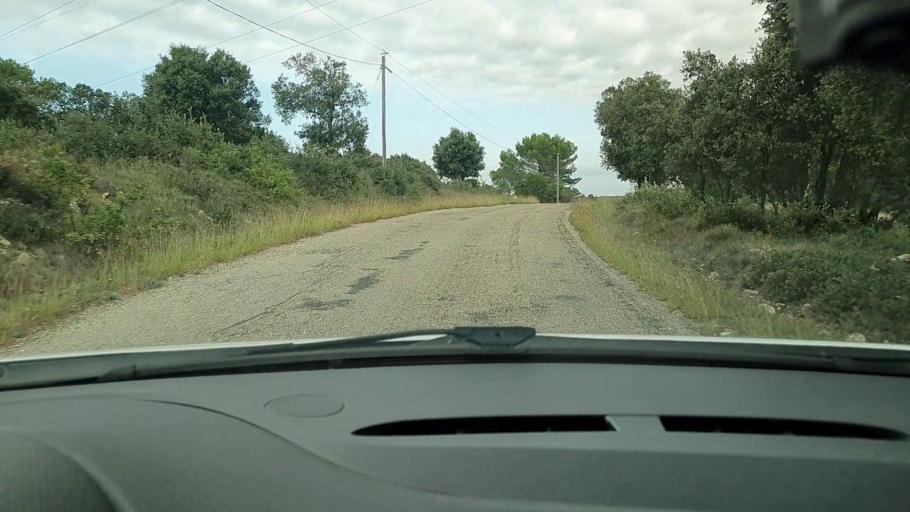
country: FR
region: Languedoc-Roussillon
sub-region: Departement du Gard
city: Montaren-et-Saint-Mediers
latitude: 44.0830
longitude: 4.2990
